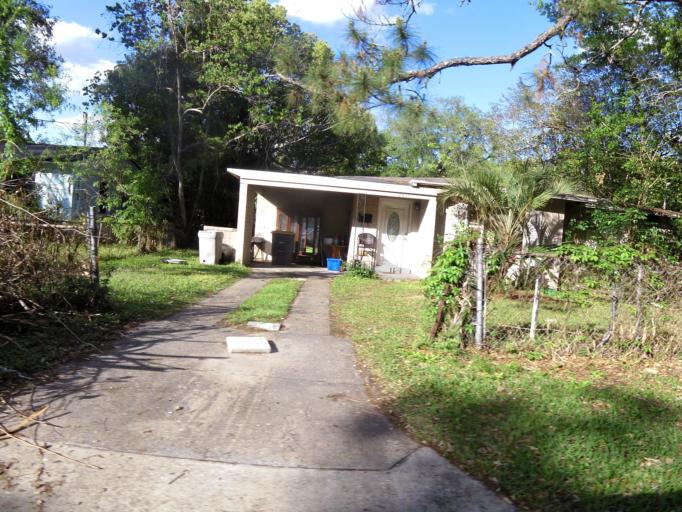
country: US
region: Florida
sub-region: Duval County
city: Jacksonville
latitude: 30.3167
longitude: -81.7013
